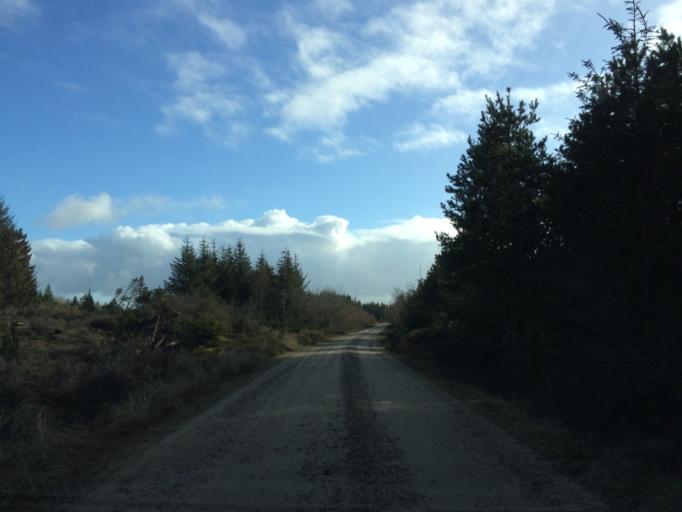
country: DK
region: Central Jutland
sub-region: Holstebro Kommune
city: Ulfborg
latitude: 56.2772
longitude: 8.3697
